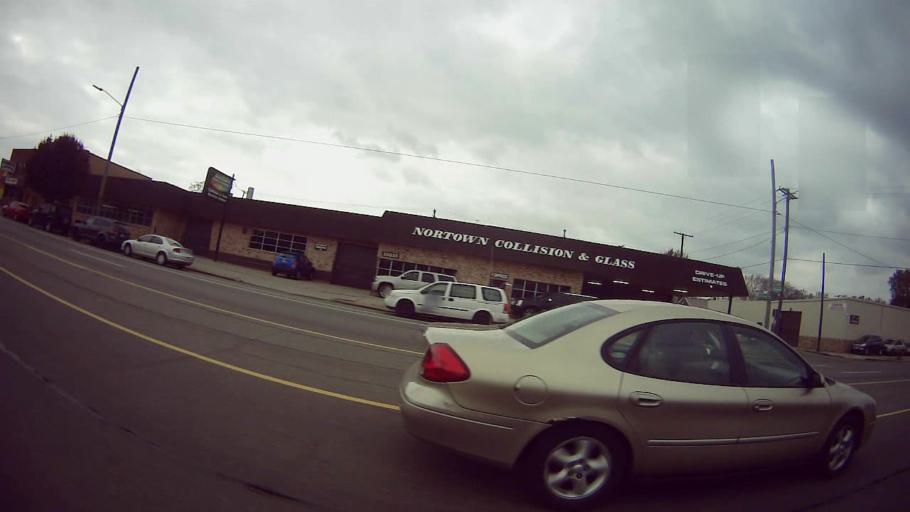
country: US
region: Michigan
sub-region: Macomb County
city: Warren
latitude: 42.4434
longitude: -83.0245
